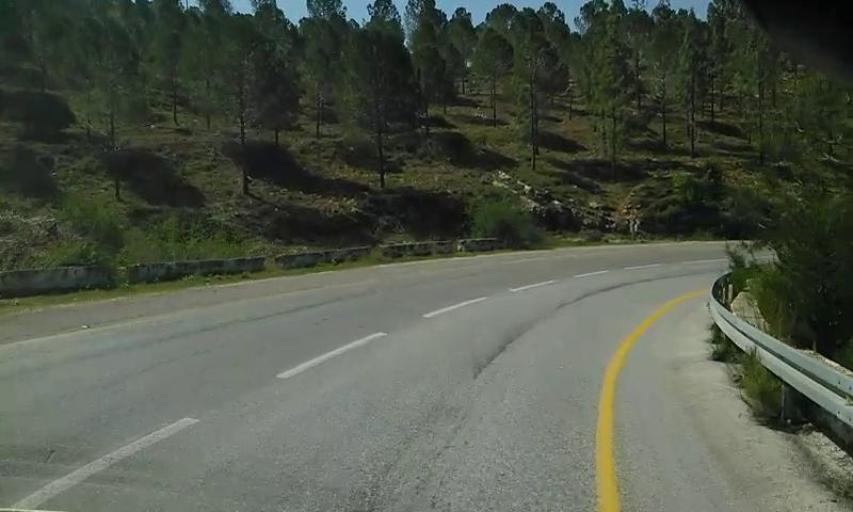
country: PS
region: West Bank
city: Nahhalin
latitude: 31.6732
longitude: 35.1047
